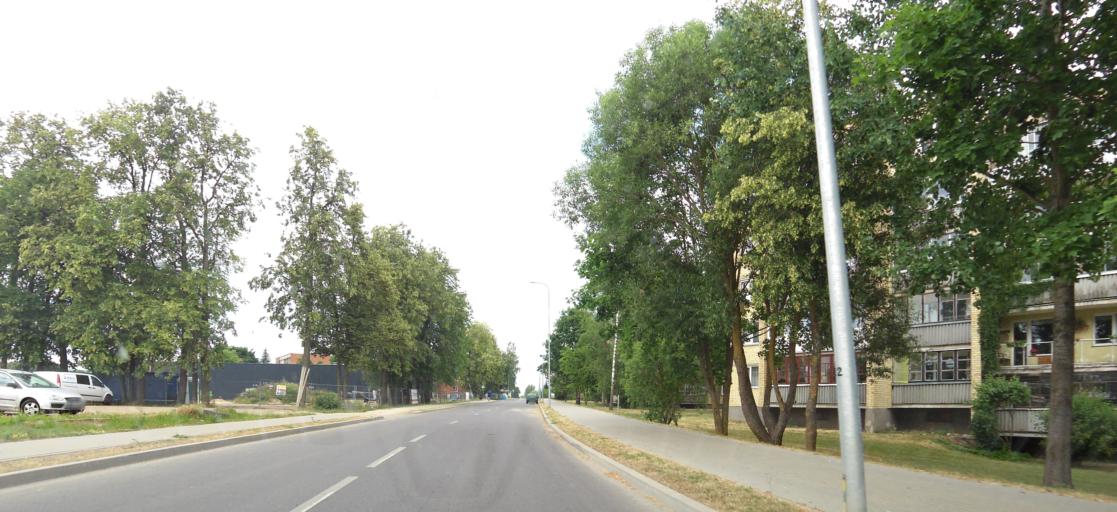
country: LT
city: Sirvintos
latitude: 55.0472
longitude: 24.9581
